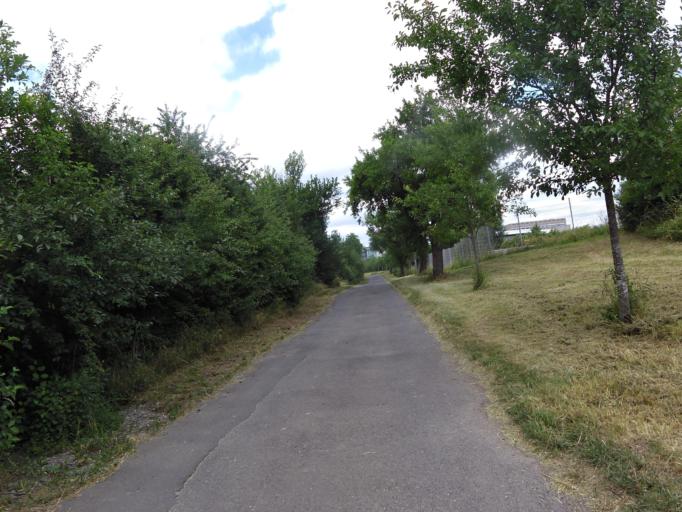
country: DE
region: Bavaria
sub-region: Regierungsbezirk Unterfranken
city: Randersacker
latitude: 49.7761
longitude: 9.9673
